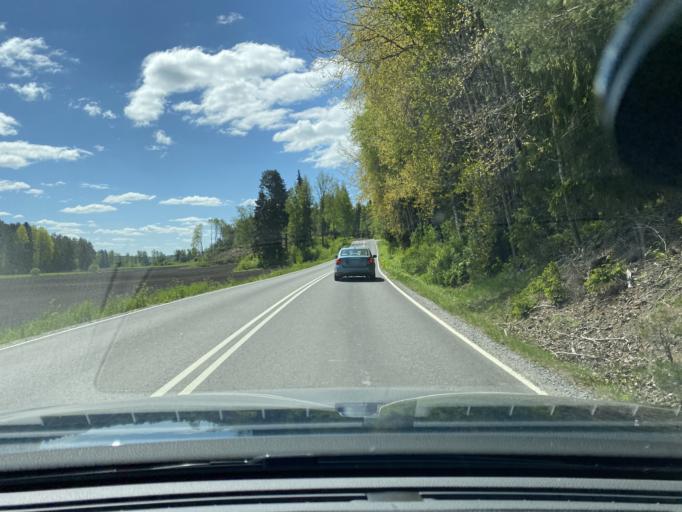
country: FI
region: Varsinais-Suomi
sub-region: Salo
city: Halikko
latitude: 60.3333
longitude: 22.9420
